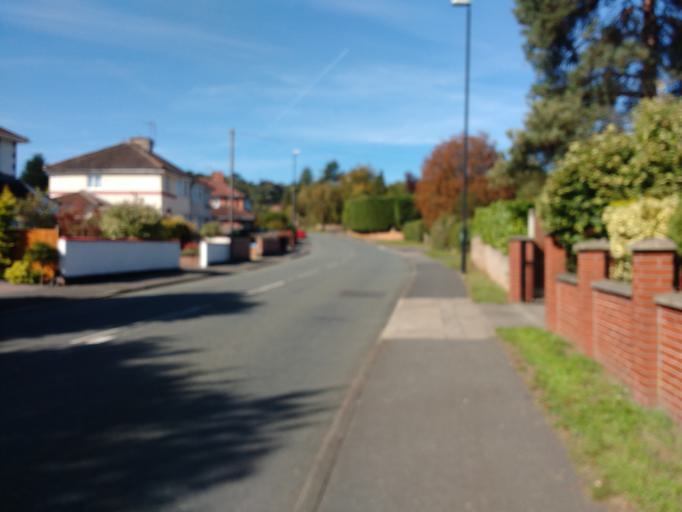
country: GB
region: England
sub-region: North Somerset
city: Easton-in-Gordano
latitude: 51.4926
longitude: -2.6438
